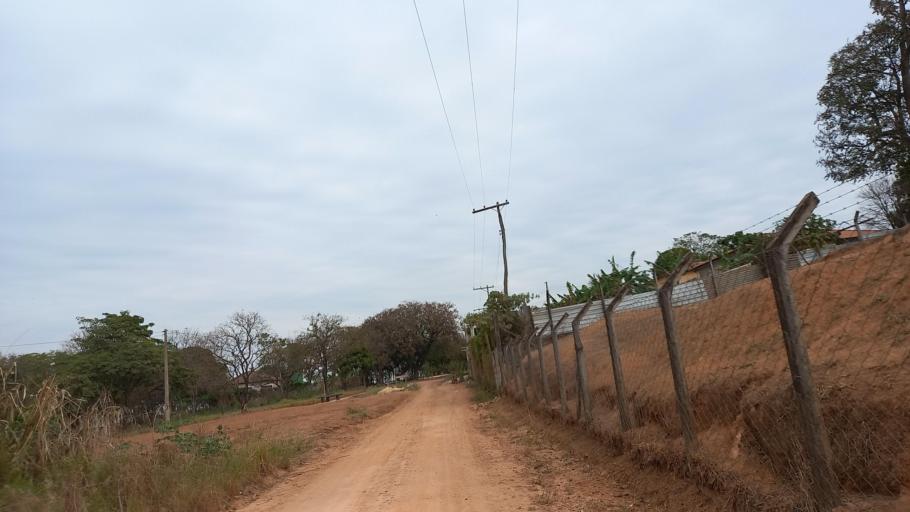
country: BR
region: Sao Paulo
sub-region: Moji-Guacu
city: Mogi-Gaucu
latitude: -22.2723
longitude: -46.8485
